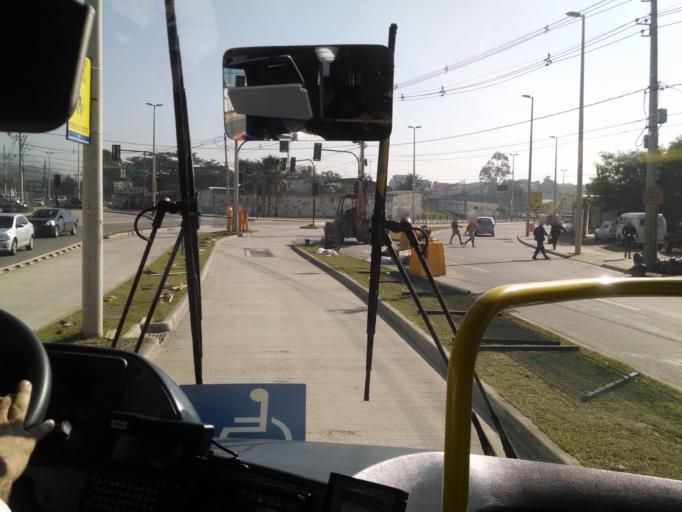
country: BR
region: Rio de Janeiro
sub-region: Nilopolis
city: Nilopolis
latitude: -22.9621
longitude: -43.3902
